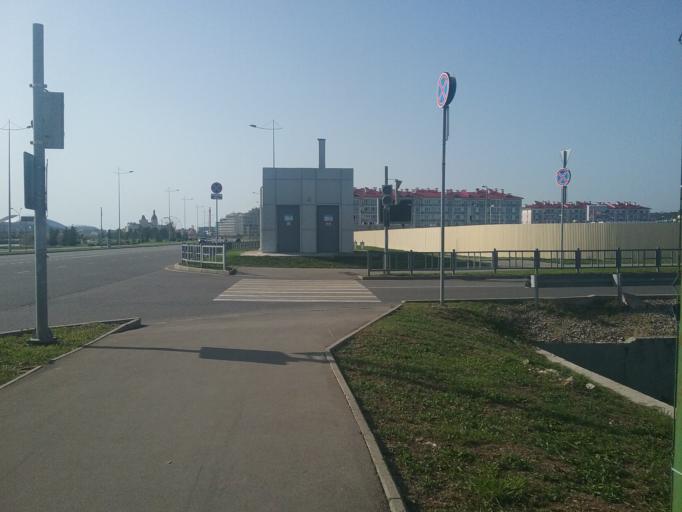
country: RU
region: Krasnodarskiy
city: Vysokoye
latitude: 43.3984
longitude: 39.9836
